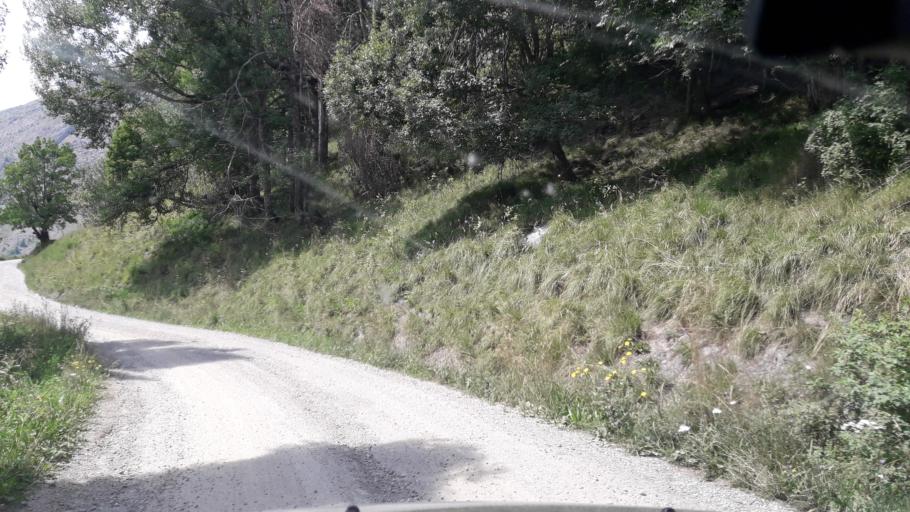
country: FR
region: Rhone-Alpes
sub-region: Departement de l'Isere
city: Mont-de-Lans
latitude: 45.0740
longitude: 6.1675
